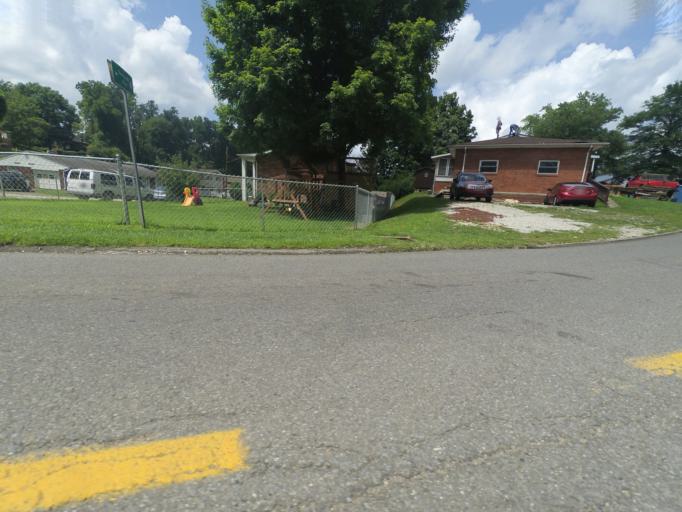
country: US
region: West Virginia
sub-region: Cabell County
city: Pea Ridge
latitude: 38.4026
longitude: -82.3806
